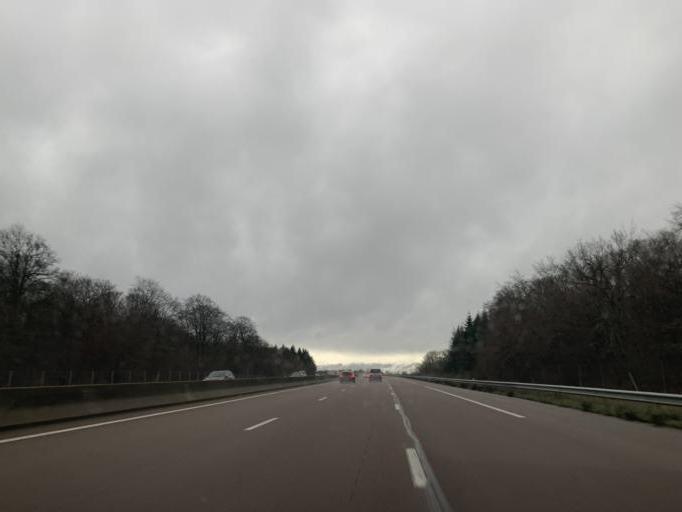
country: FR
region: Bourgogne
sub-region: Departement de la Cote-d'Or
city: Selongey
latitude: 47.6326
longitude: 5.1802
